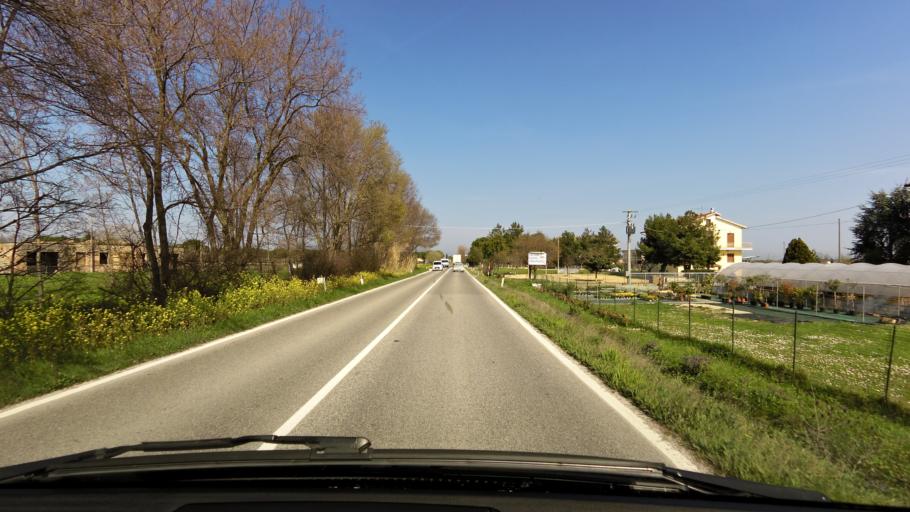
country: IT
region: The Marches
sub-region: Provincia di Macerata
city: Porto Recanati
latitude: 43.3969
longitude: 13.6491
